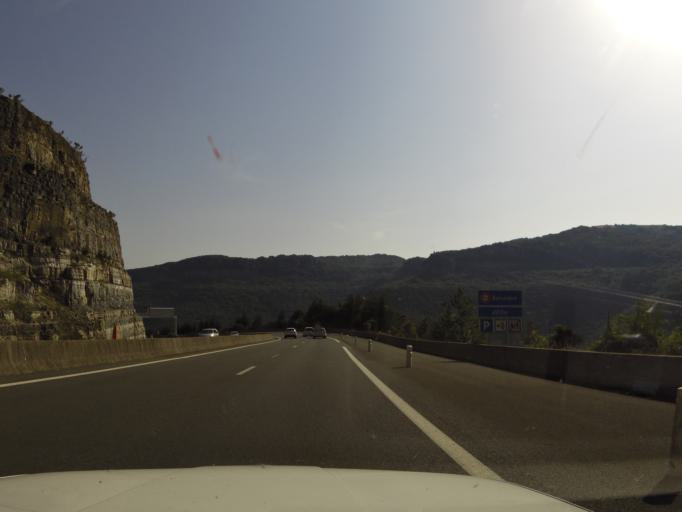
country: FR
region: Languedoc-Roussillon
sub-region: Departement de l'Herault
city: Lodeve
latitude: 43.8212
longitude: 3.3197
